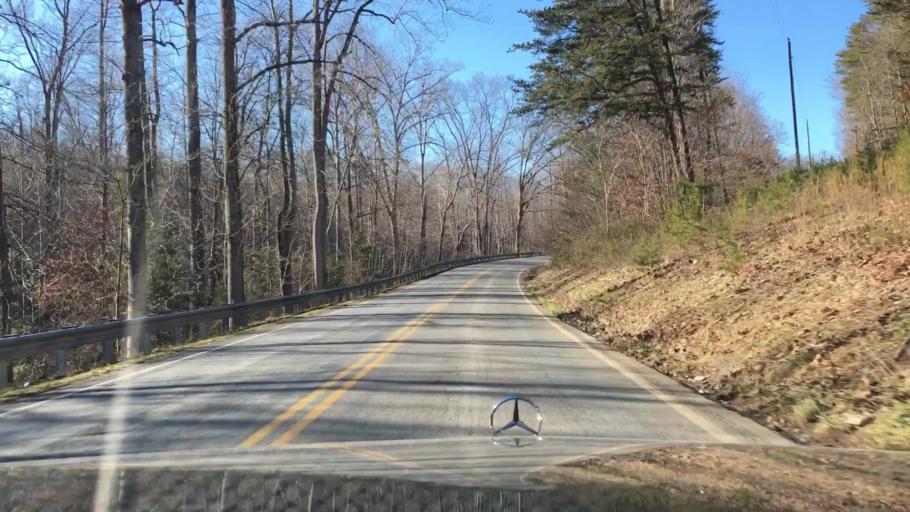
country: US
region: Virginia
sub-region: Pittsylvania County
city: Motley
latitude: 37.1556
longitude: -79.3925
